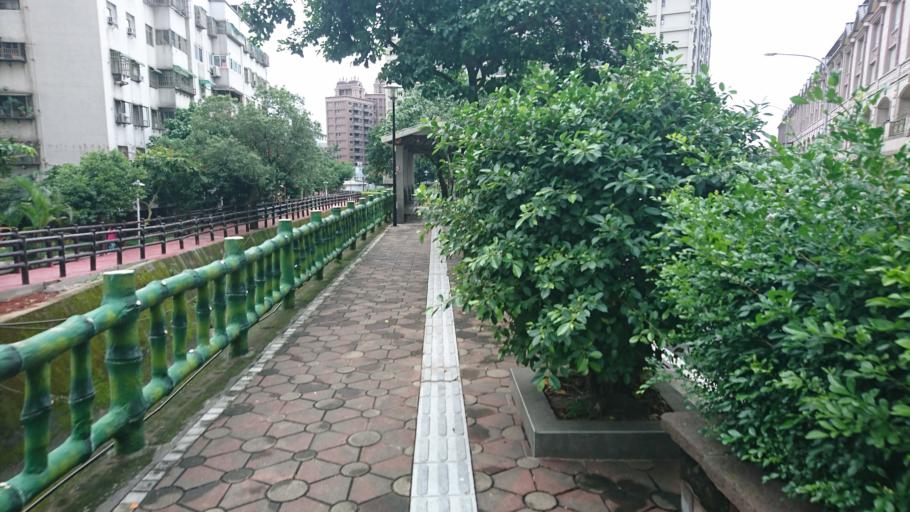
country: TW
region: Taiwan
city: Taoyuan City
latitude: 25.0606
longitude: 121.2967
